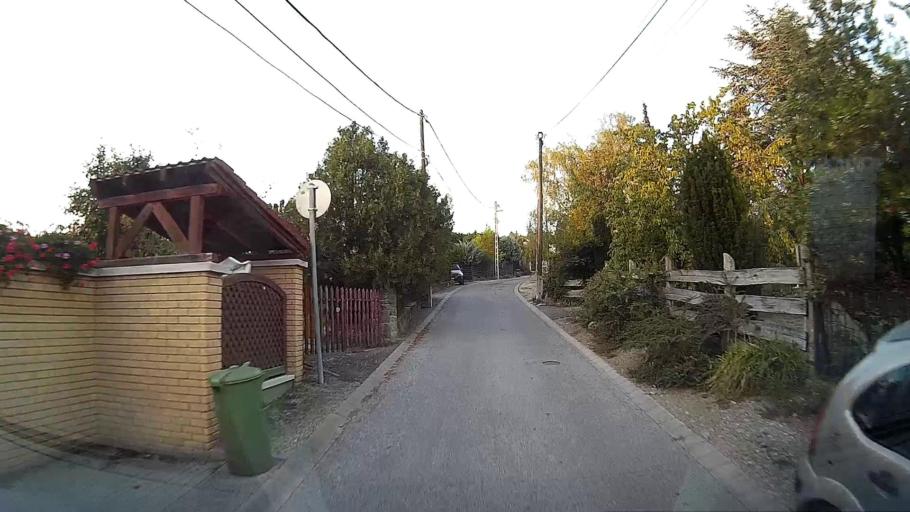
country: HU
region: Pest
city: Szentendre
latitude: 47.6911
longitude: 19.0614
